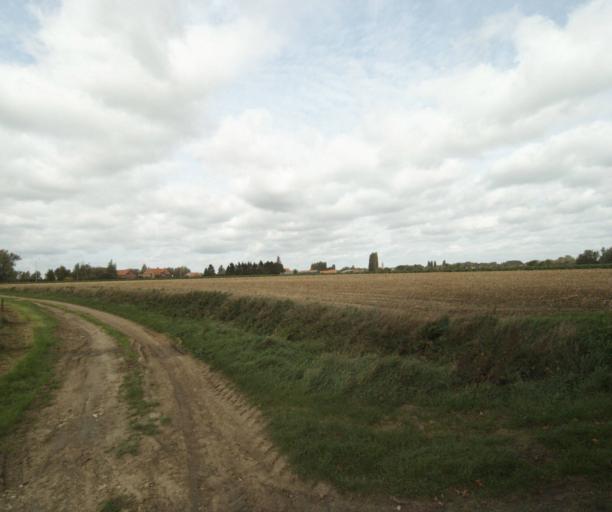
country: FR
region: Nord-Pas-de-Calais
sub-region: Departement du Nord
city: Erquinghem-Lys
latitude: 50.6664
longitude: 2.8481
